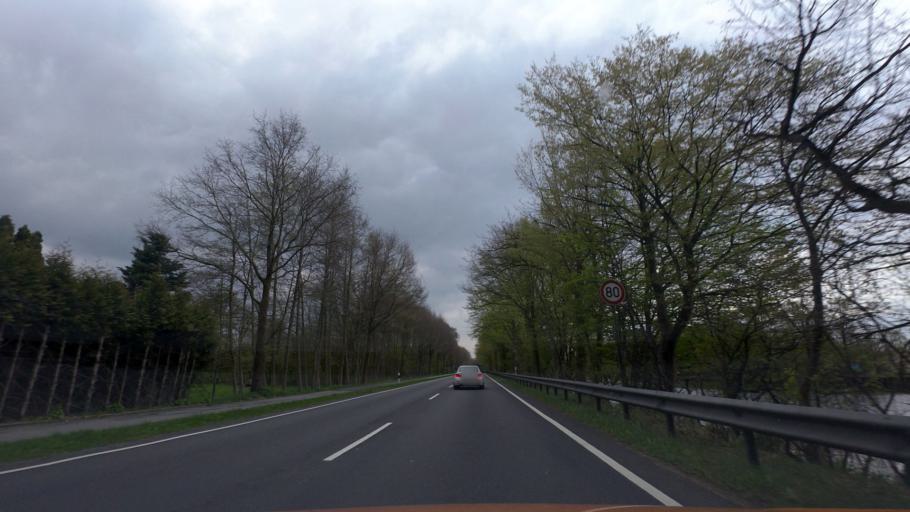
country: DE
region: Lower Saxony
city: Wardenburg
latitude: 53.1091
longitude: 8.1663
